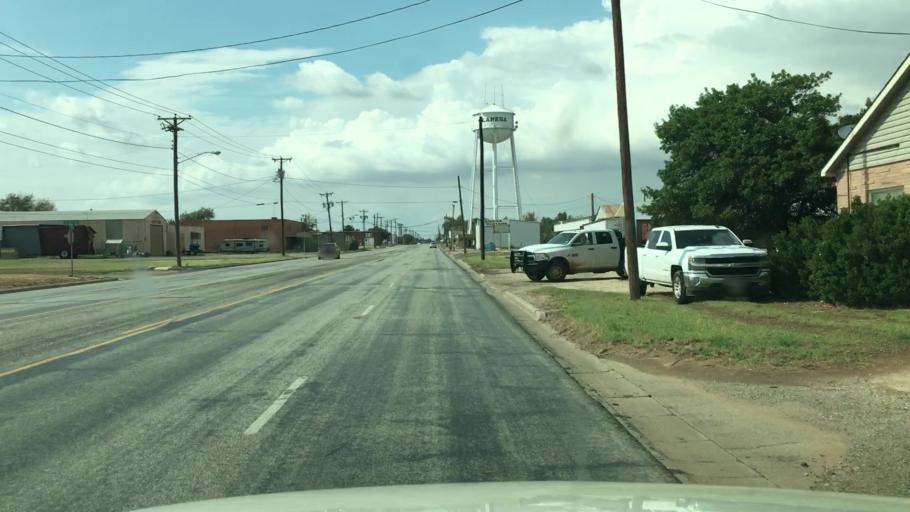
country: US
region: Texas
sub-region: Dawson County
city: Lamesa
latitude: 32.7282
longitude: -101.9476
